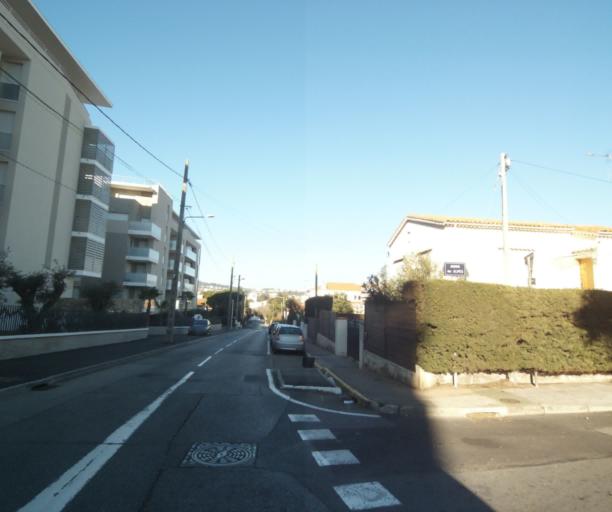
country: FR
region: Provence-Alpes-Cote d'Azur
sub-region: Departement des Alpes-Maritimes
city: Antibes
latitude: 43.5835
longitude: 7.1076
